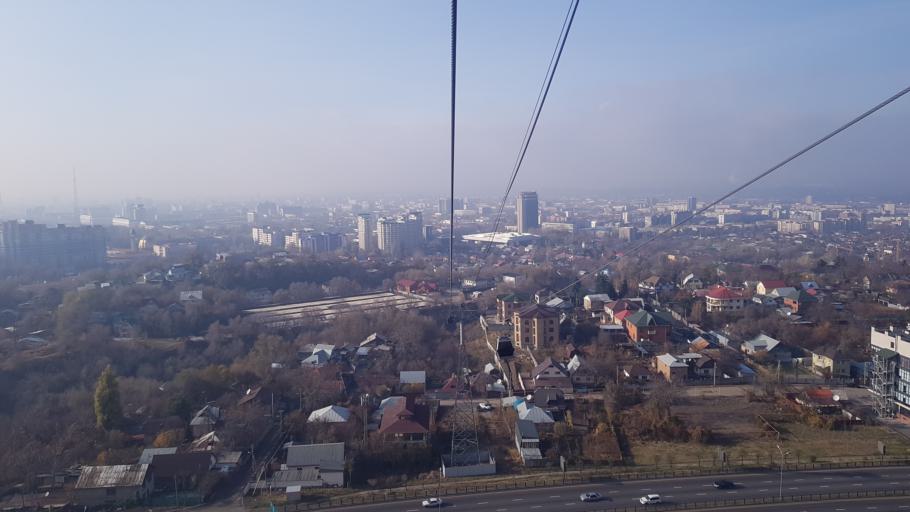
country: KZ
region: Almaty Qalasy
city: Almaty
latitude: 43.2360
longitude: 76.9720
